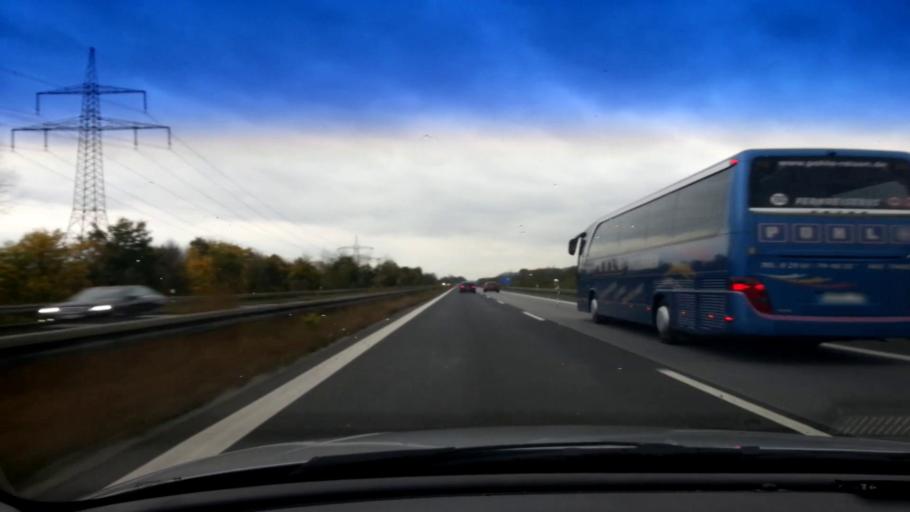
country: DE
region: Bavaria
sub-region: Regierungsbezirk Unterfranken
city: Stettfeld
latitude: 49.9734
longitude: 10.6979
